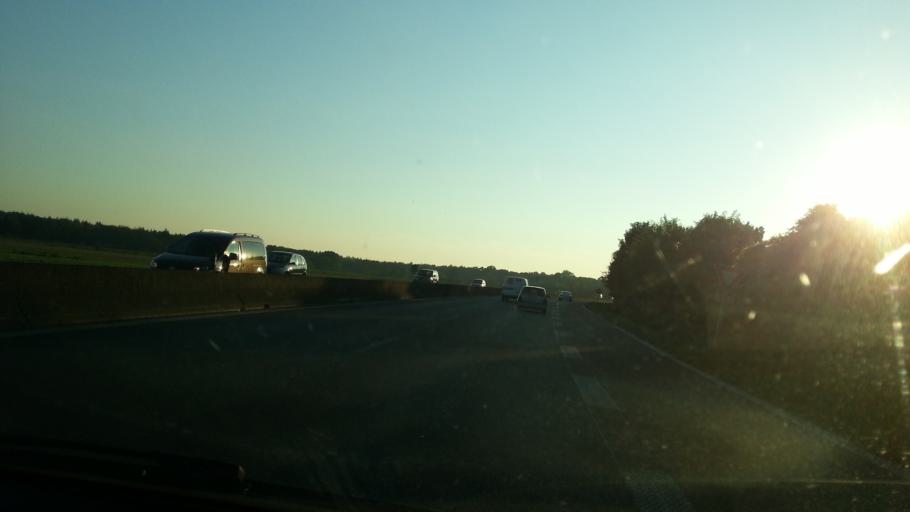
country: FR
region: Picardie
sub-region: Departement de l'Oise
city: Creil
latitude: 49.2519
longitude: 2.4894
